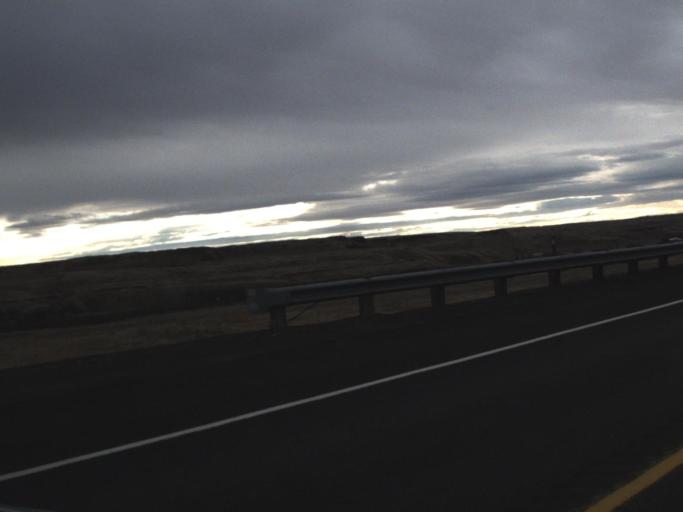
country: US
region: Washington
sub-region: Adams County
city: Ritzville
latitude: 46.7563
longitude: -118.1745
